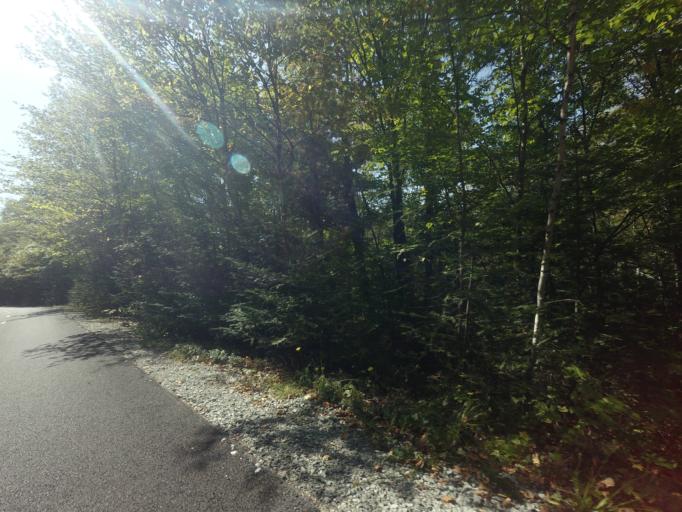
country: CA
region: Quebec
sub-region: Laurentides
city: Mont-Tremblant
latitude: 46.1292
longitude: -74.4937
